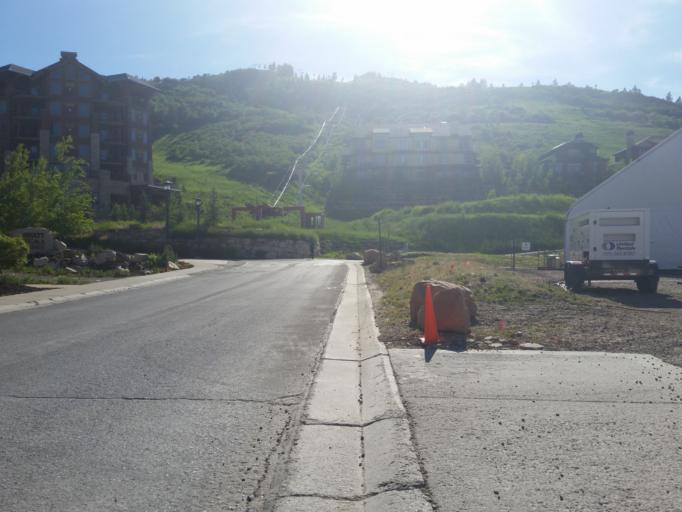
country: US
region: Utah
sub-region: Summit County
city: Snyderville
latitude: 40.6833
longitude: -111.5556
